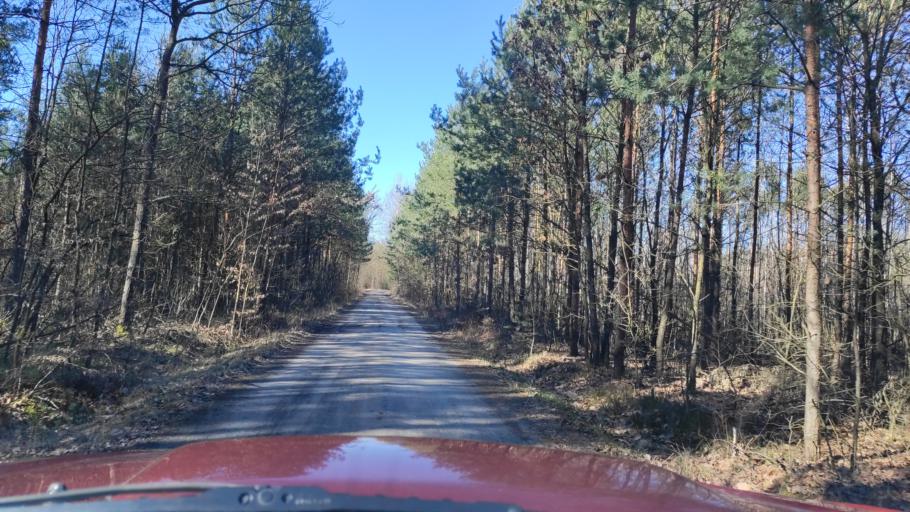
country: PL
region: Masovian Voivodeship
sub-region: Powiat kozienicki
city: Garbatka-Letnisko
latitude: 51.4414
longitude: 21.5392
